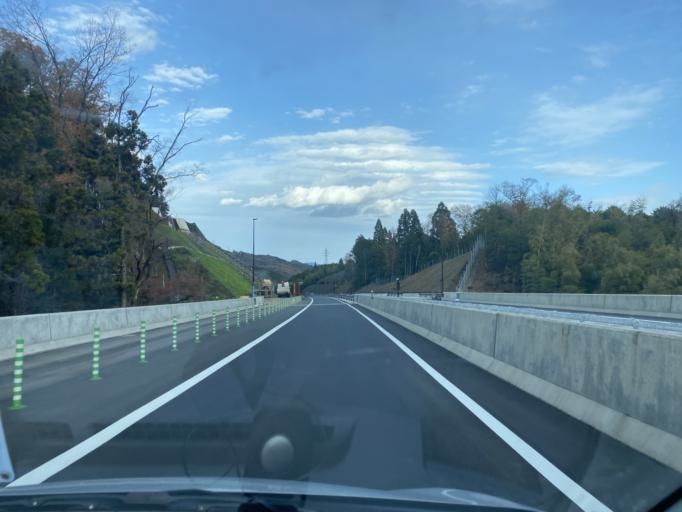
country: JP
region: Hyogo
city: Toyooka
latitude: 35.4878
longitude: 134.7766
